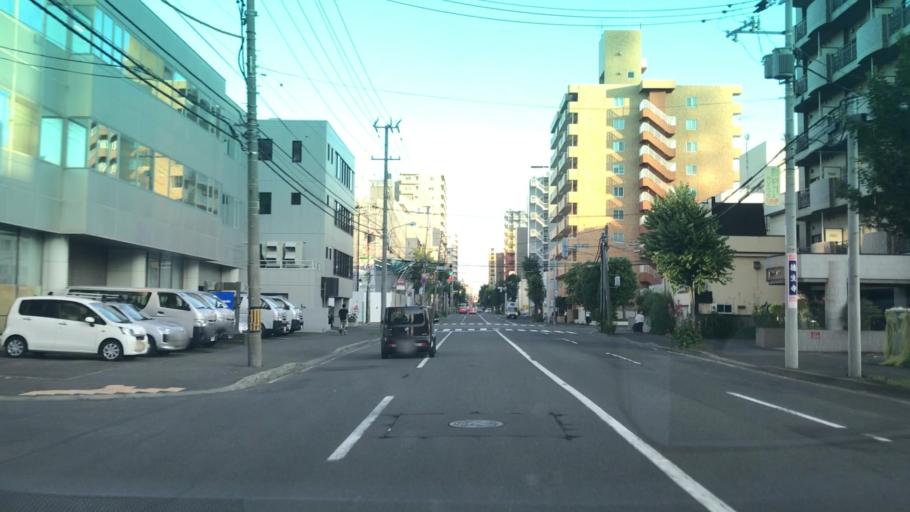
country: JP
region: Hokkaido
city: Sapporo
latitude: 43.0667
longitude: 141.3360
